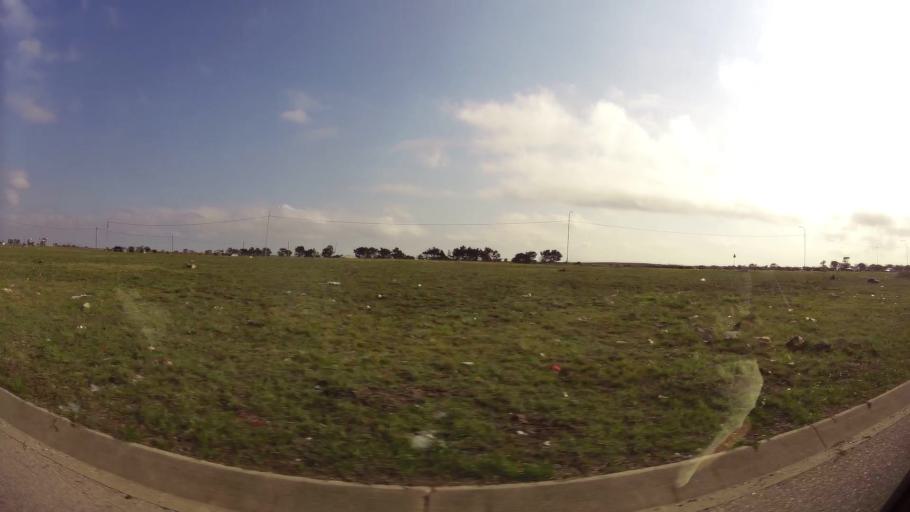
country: ZA
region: Eastern Cape
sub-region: Nelson Mandela Bay Metropolitan Municipality
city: Port Elizabeth
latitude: -33.9187
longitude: 25.5309
